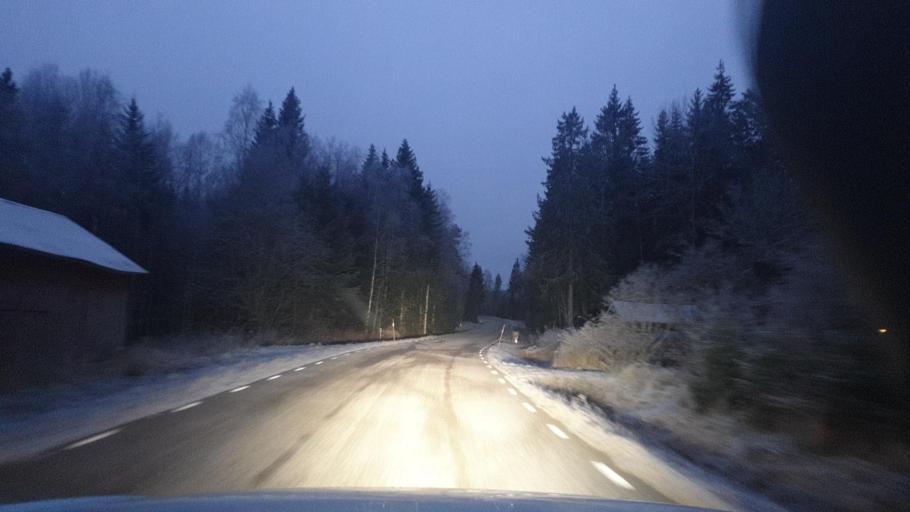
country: SE
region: Vaermland
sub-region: Arvika Kommun
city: Arvika
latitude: 59.5565
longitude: 12.4238
